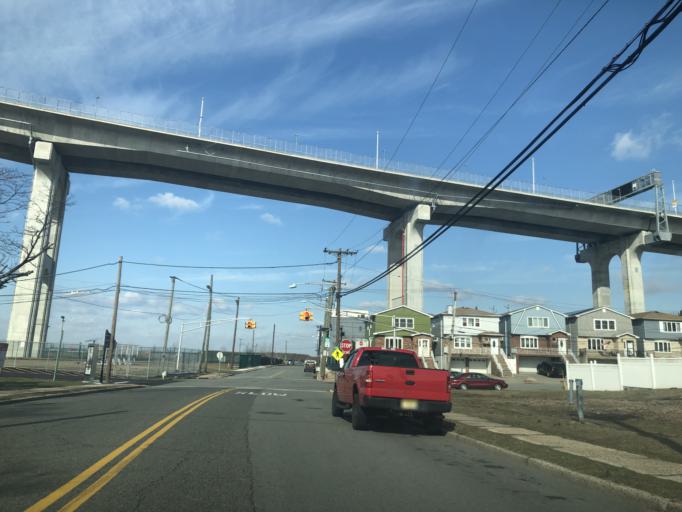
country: US
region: New Jersey
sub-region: Hudson County
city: Bayonne
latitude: 40.6465
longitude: -74.1388
